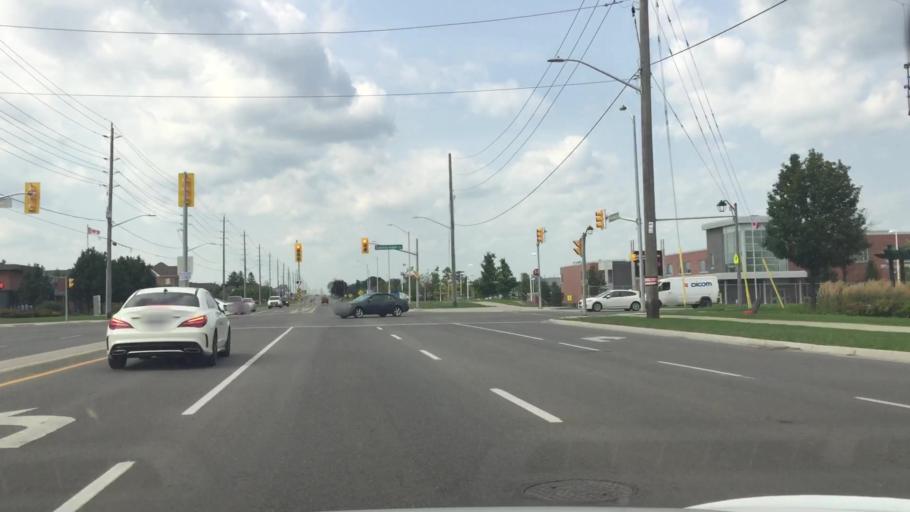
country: CA
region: Ontario
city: Oshawa
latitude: 43.9441
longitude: -78.8514
